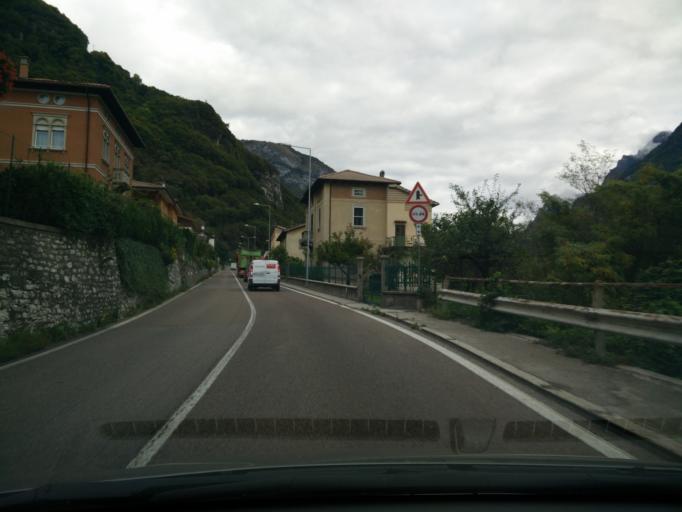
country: IT
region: Veneto
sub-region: Provincia di Belluno
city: Longarone
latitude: 46.2740
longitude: 12.3010
